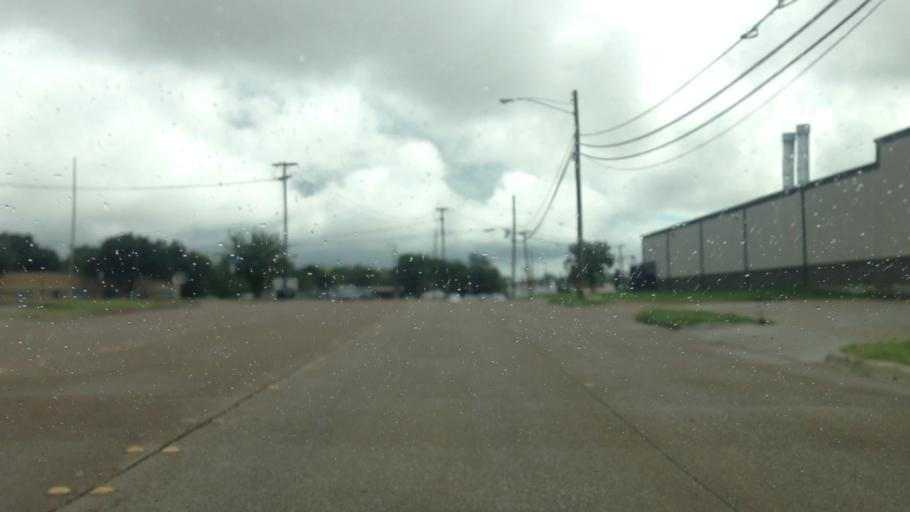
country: US
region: Texas
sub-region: Tarrant County
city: White Settlement
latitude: 32.7556
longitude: -97.4511
